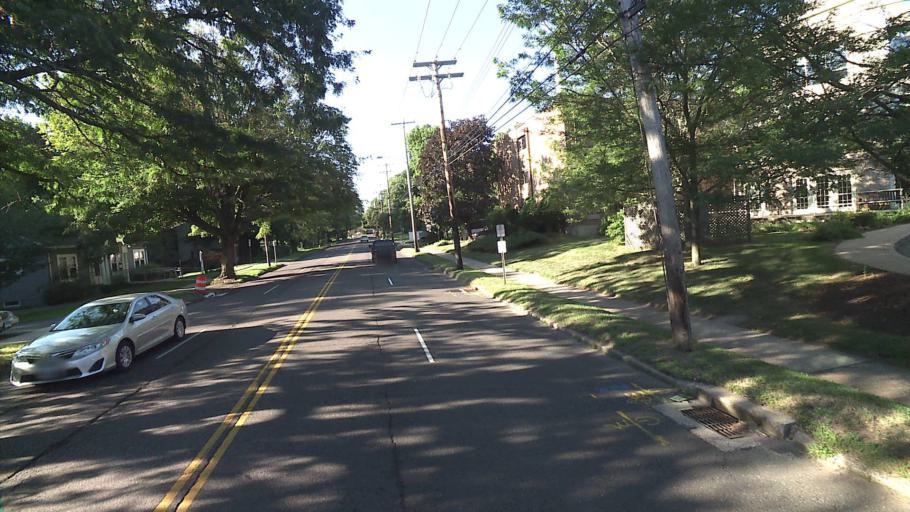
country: US
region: Connecticut
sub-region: New Haven County
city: Hamden
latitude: 41.3983
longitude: -72.8973
